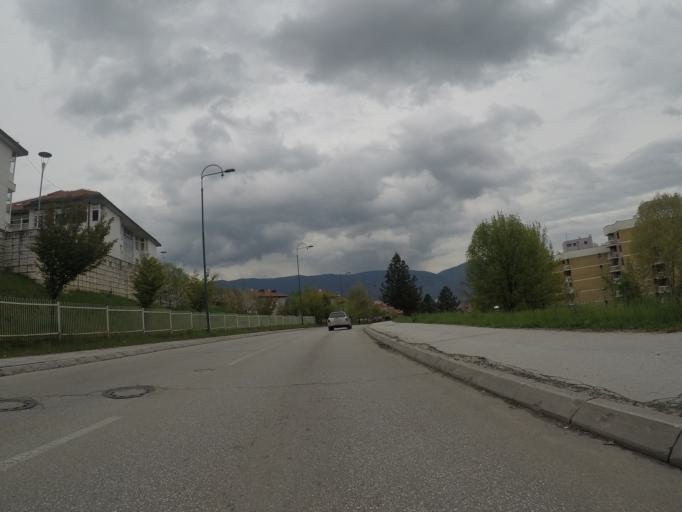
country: BA
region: Federation of Bosnia and Herzegovina
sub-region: Kanton Sarajevo
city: Sarajevo
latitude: 43.8373
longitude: 18.3481
